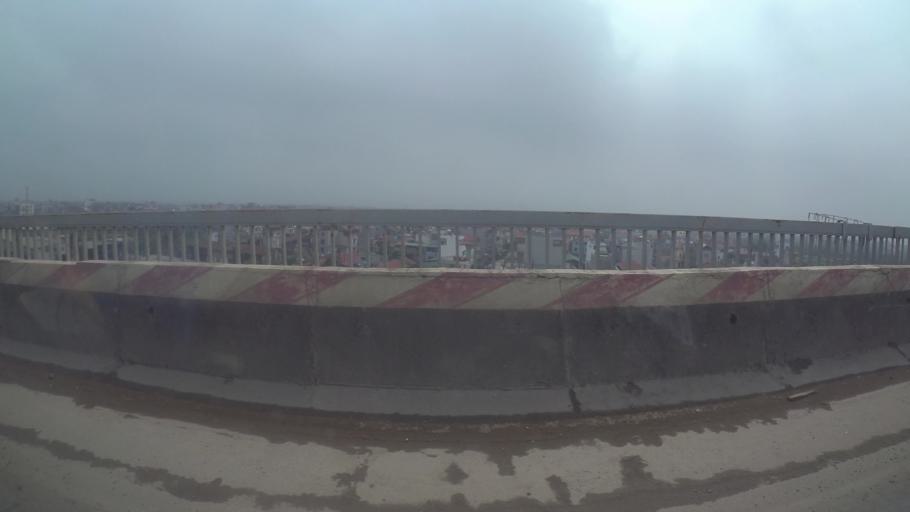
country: VN
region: Ha Noi
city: Tay Ho
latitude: 21.1087
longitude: 105.7871
